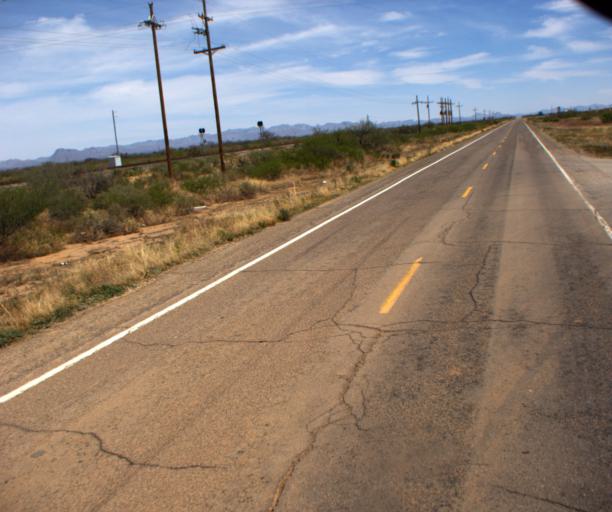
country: US
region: Arizona
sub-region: Cochise County
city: Willcox
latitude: 32.3217
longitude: -109.4588
